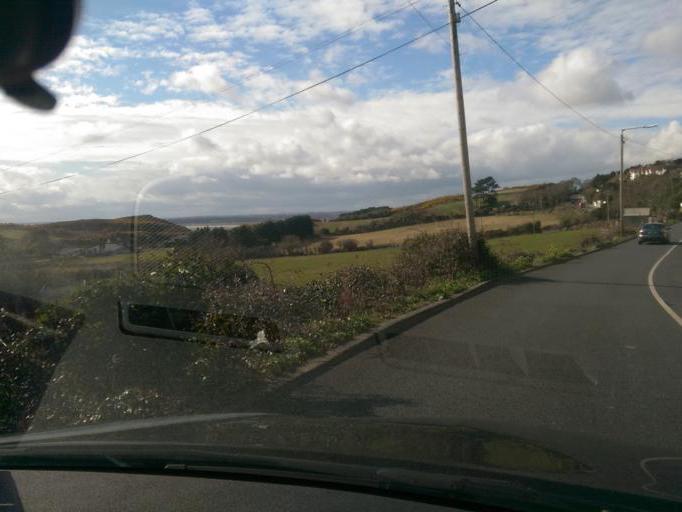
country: IE
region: Leinster
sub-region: Fingal County
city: Howth
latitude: 53.3675
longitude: -6.0804
